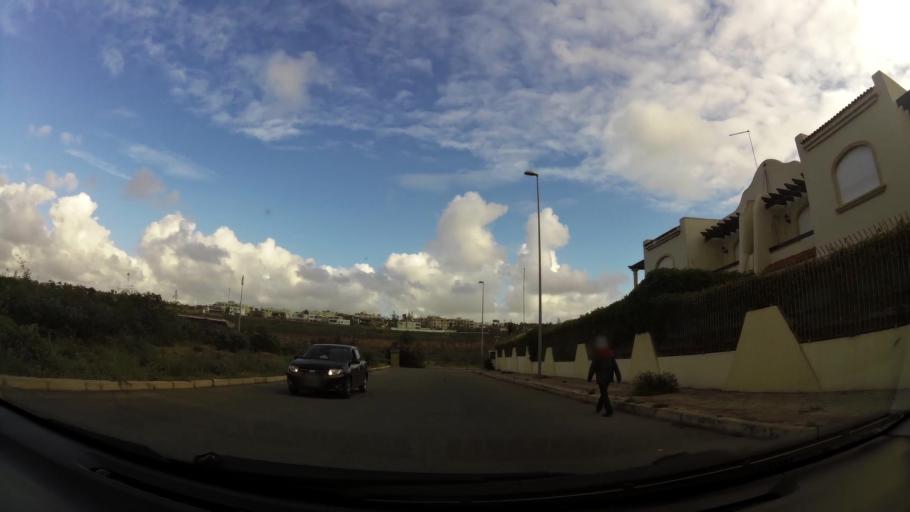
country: MA
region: Grand Casablanca
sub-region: Casablanca
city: Casablanca
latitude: 33.5783
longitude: -7.6921
